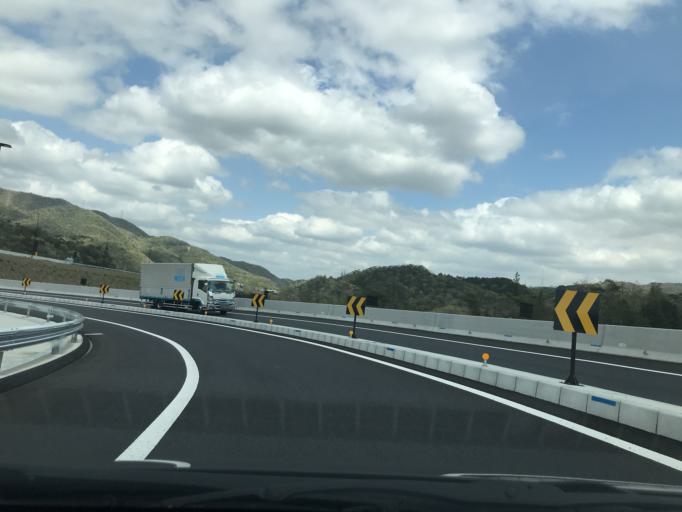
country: JP
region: Hyogo
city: Sandacho
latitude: 34.8646
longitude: 135.3059
